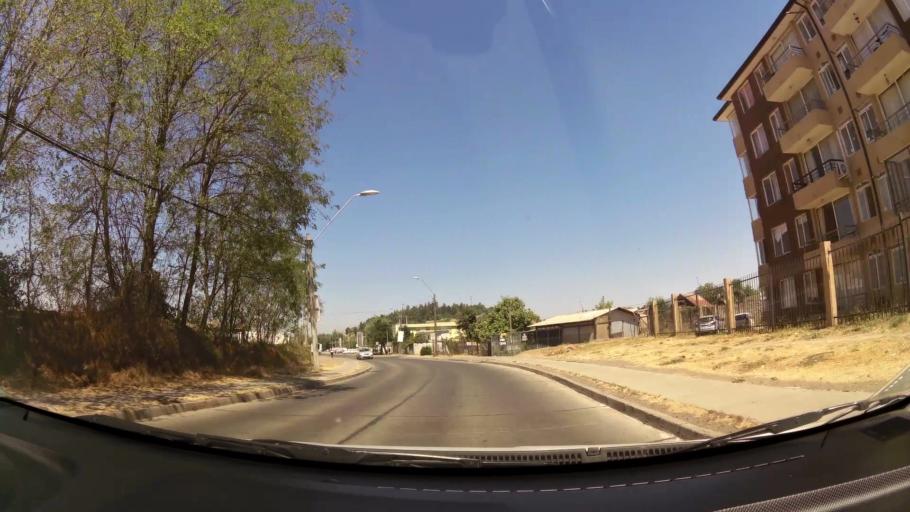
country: CL
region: Maule
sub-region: Provincia de Curico
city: Curico
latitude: -34.9730
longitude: -71.2199
